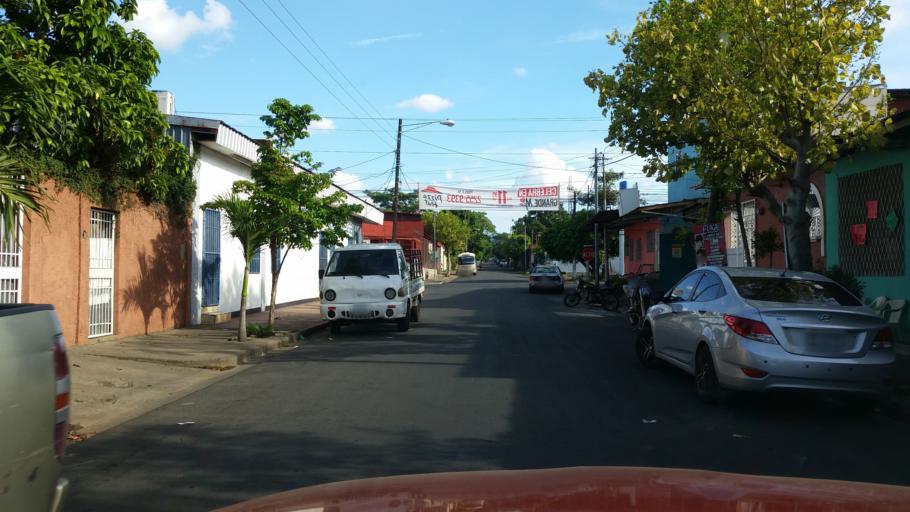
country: NI
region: Managua
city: Managua
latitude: 12.1462
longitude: -86.2812
